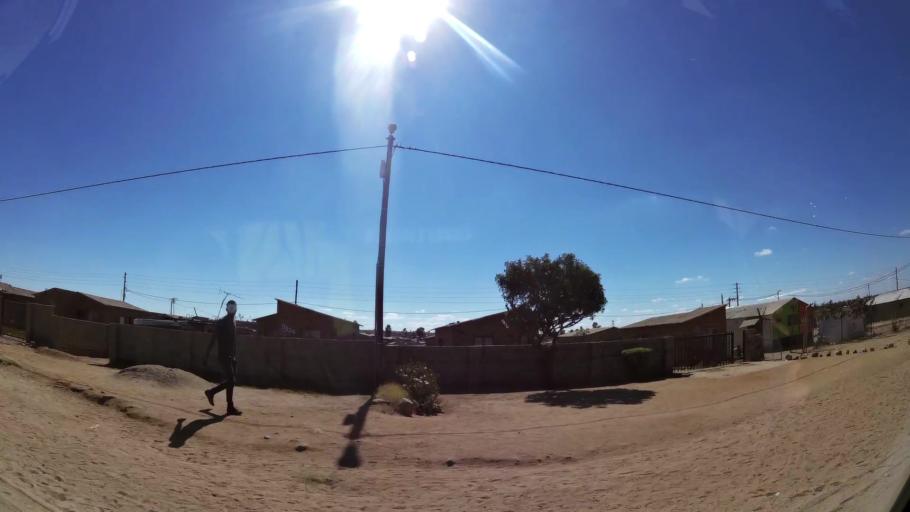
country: ZA
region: Limpopo
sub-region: Capricorn District Municipality
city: Polokwane
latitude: -23.8912
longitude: 29.4205
